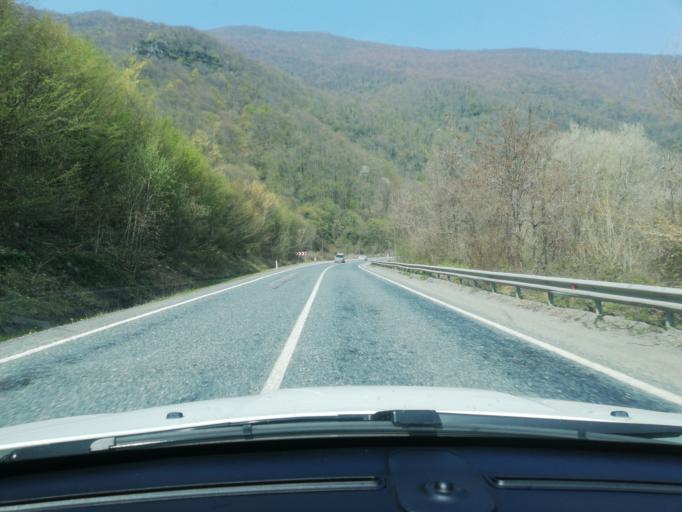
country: TR
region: Zonguldak
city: Gokcebey
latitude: 41.2637
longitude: 32.1573
